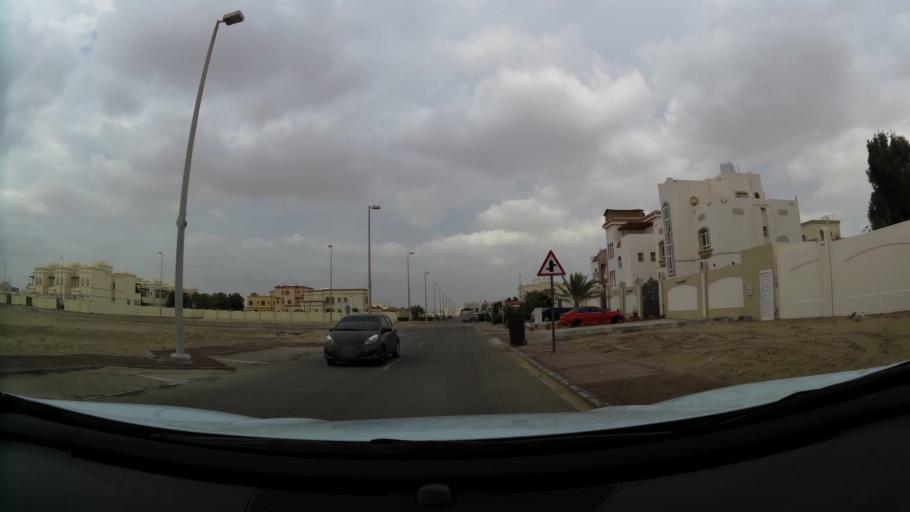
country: AE
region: Abu Dhabi
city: Abu Dhabi
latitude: 24.3434
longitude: 54.6188
